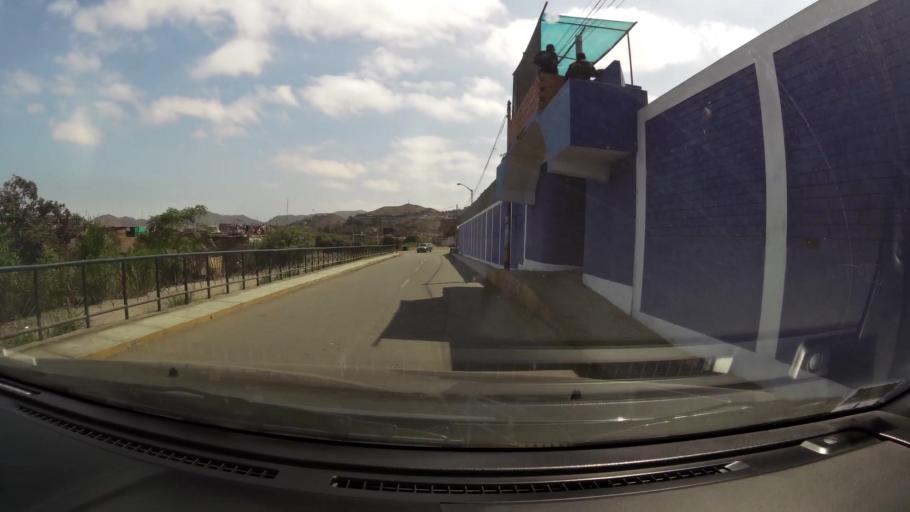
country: PE
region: Lima
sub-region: Provincia de Canete
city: Mala
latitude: -12.6560
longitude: -76.6294
